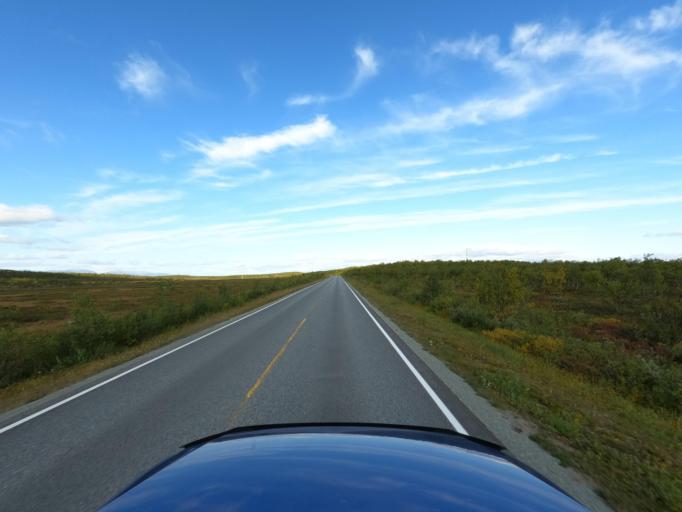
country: NO
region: Finnmark Fylke
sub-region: Karasjok
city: Karasjohka
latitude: 69.6967
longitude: 25.2573
